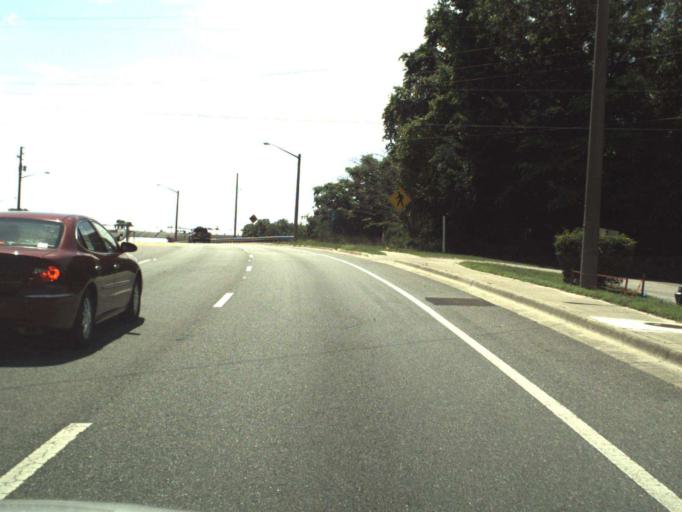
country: US
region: Florida
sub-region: Marion County
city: Ocala
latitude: 29.2007
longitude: -82.1273
